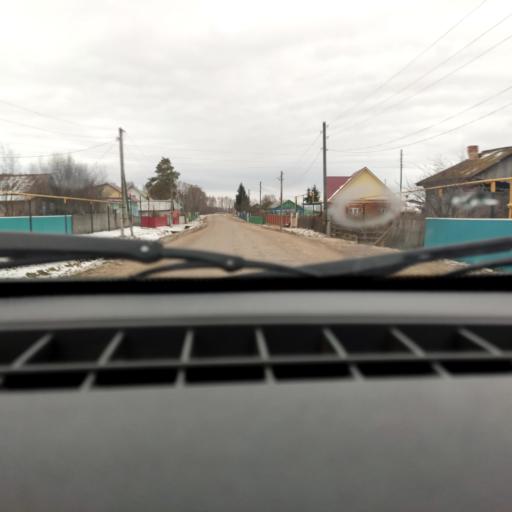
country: RU
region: Bashkortostan
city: Tolbazy
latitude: 54.2544
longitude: 55.9181
